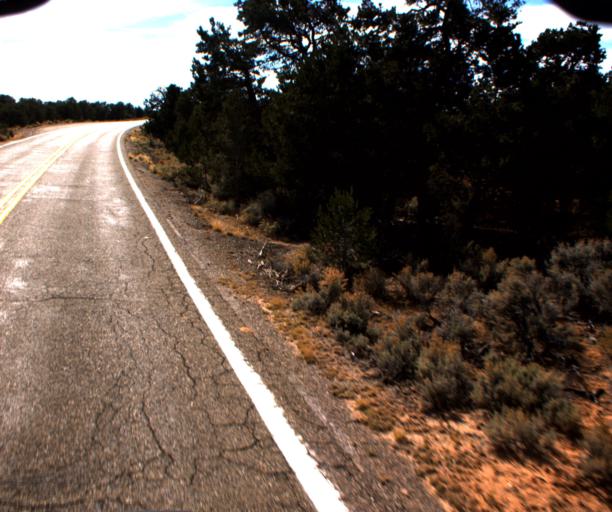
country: US
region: Arizona
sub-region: Navajo County
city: Kayenta
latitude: 36.6007
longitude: -110.4970
